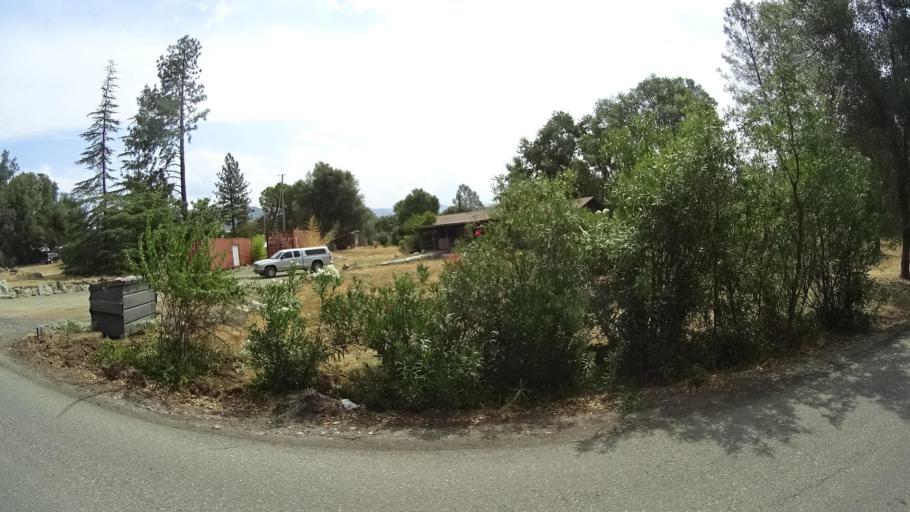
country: US
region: California
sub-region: Mariposa County
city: Midpines
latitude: 37.5050
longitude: -119.9071
